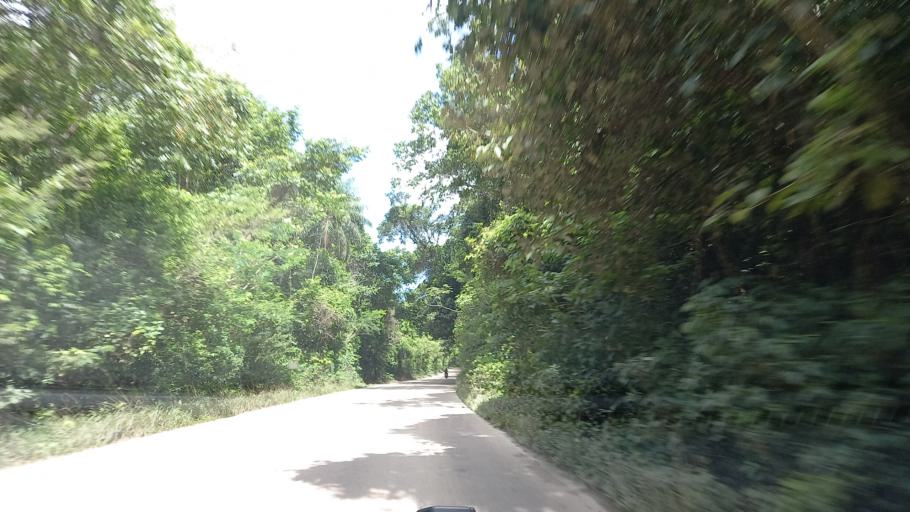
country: BR
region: Pernambuco
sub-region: Rio Formoso
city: Rio Formoso
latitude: -8.7251
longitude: -35.1730
